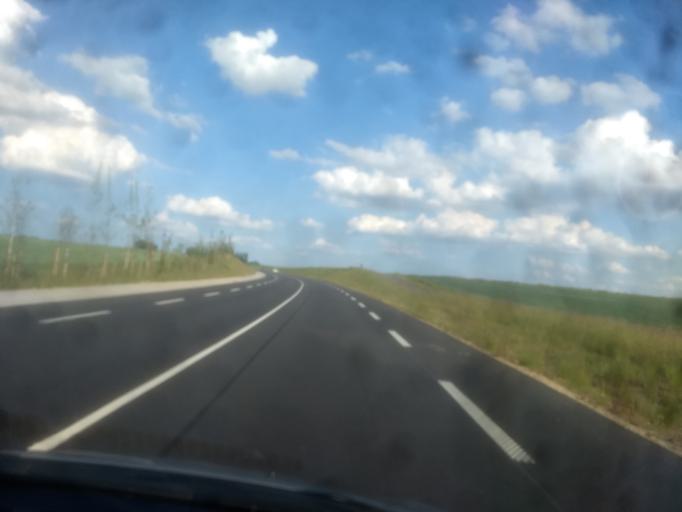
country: FR
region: Nord-Pas-de-Calais
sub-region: Departement du Pas-de-Calais
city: Agny
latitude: 50.2523
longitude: 2.7497
